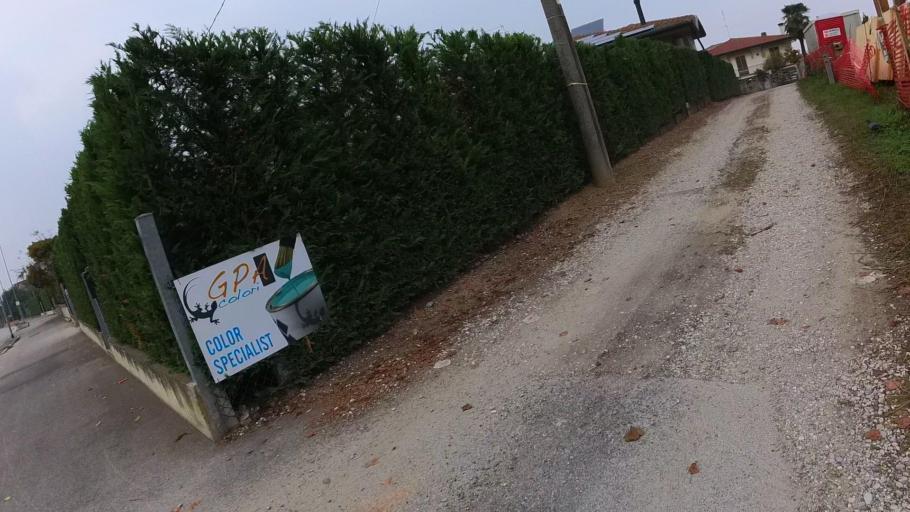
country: IT
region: Veneto
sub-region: Provincia di Venezia
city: Fosso
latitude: 45.3827
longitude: 12.0600
